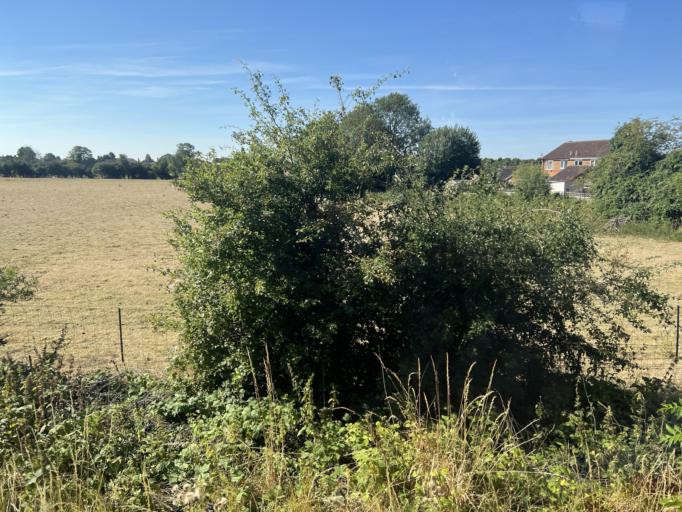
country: GB
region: England
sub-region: Lincolnshire
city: Heckington
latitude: 52.9766
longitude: -0.2907
